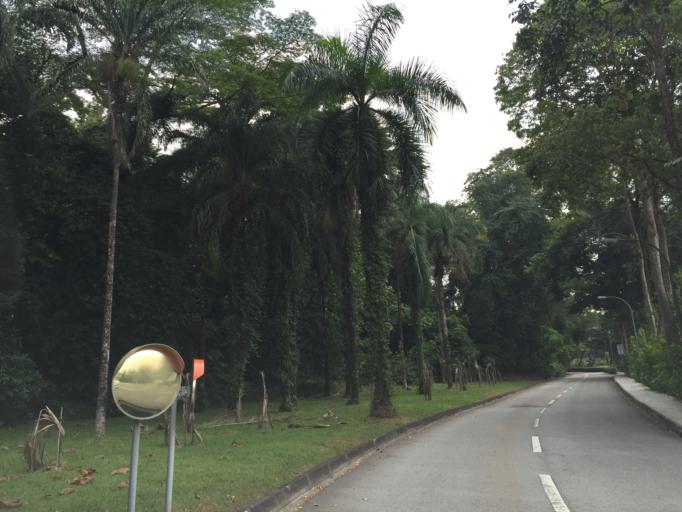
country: SG
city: Singapore
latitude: 1.3237
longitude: 103.8346
